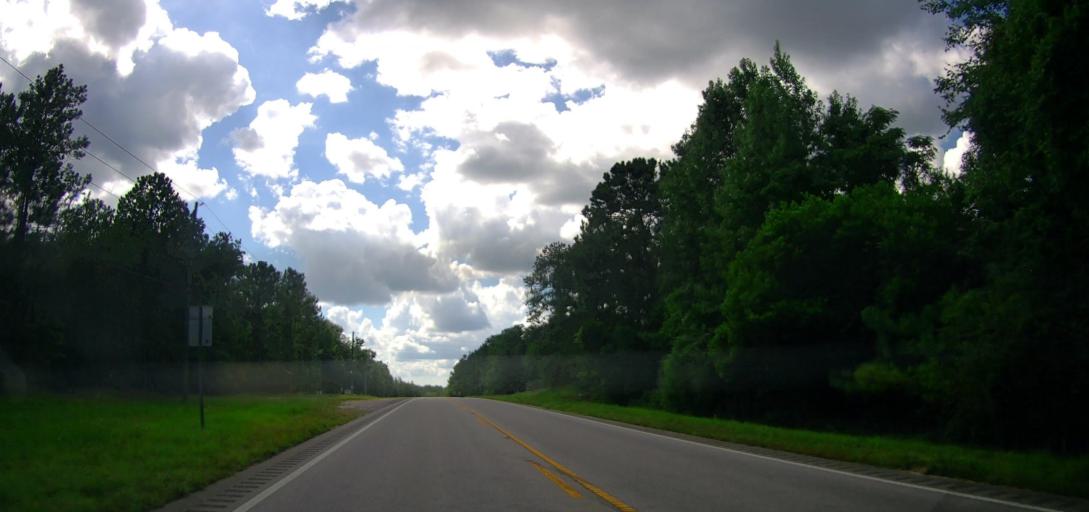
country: US
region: Alabama
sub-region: Lee County
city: Auburn
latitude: 32.4443
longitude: -85.5027
